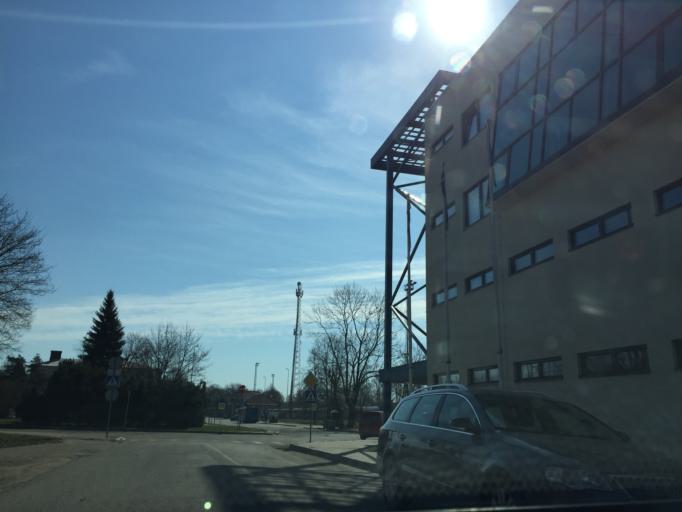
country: EE
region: Ida-Virumaa
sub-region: Narva linn
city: Narva
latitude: 59.3700
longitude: 28.1958
